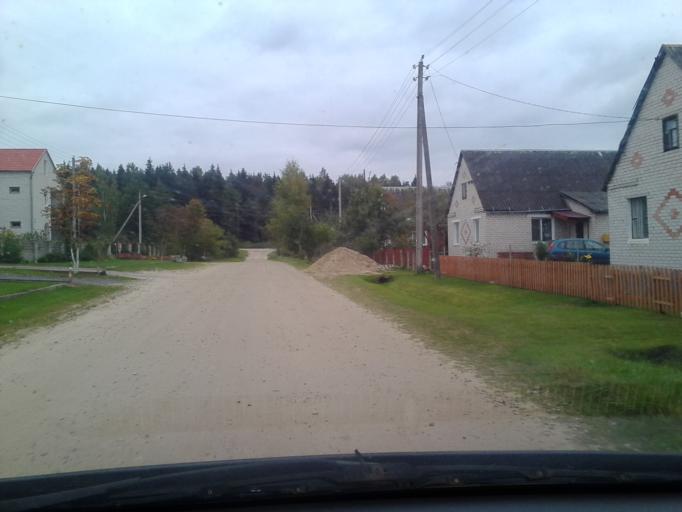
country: BY
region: Vitebsk
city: Pastavy
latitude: 55.1043
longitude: 26.8656
